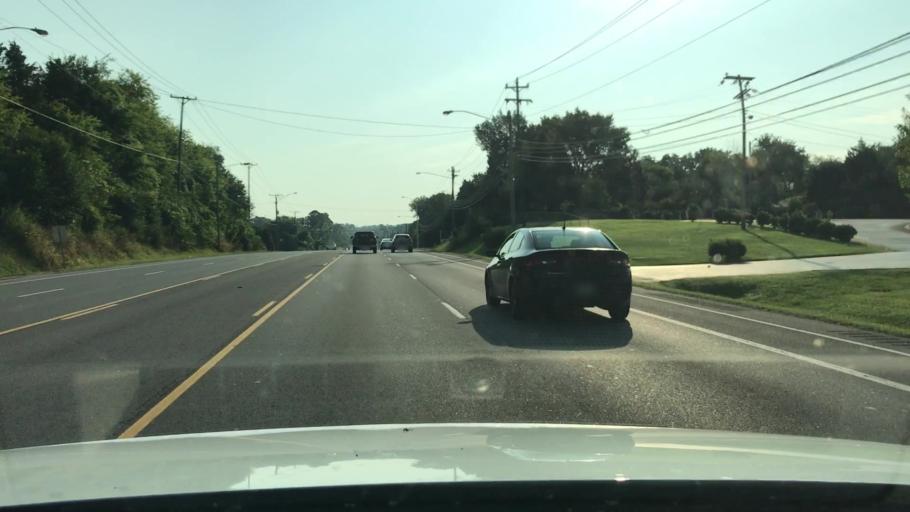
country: US
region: Tennessee
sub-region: Sumner County
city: Hendersonville
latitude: 36.3177
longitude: -86.5834
